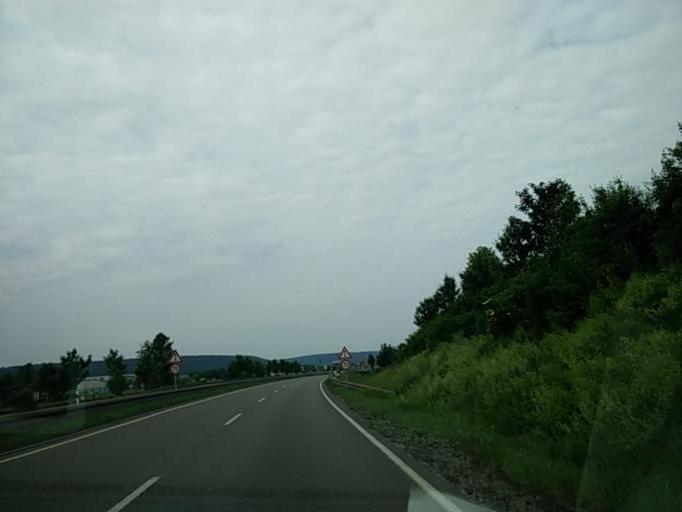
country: DE
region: Baden-Wuerttemberg
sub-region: Tuebingen Region
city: Tuebingen
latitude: 48.5027
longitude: 9.0357
